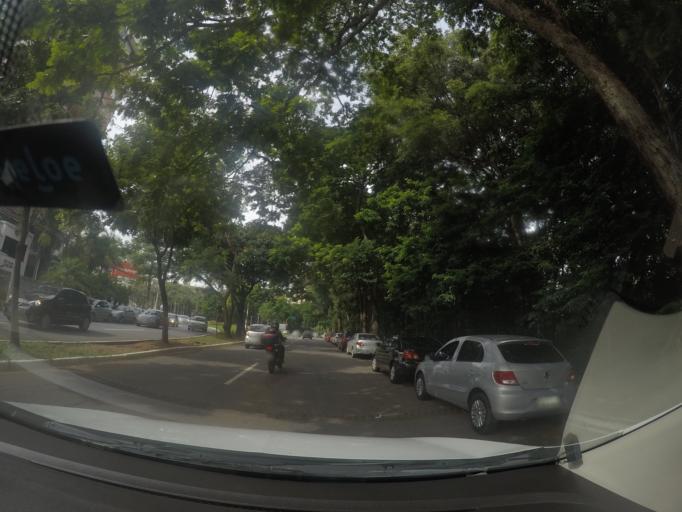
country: BR
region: Goias
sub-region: Goiania
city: Goiania
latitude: -16.6809
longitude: -49.2602
